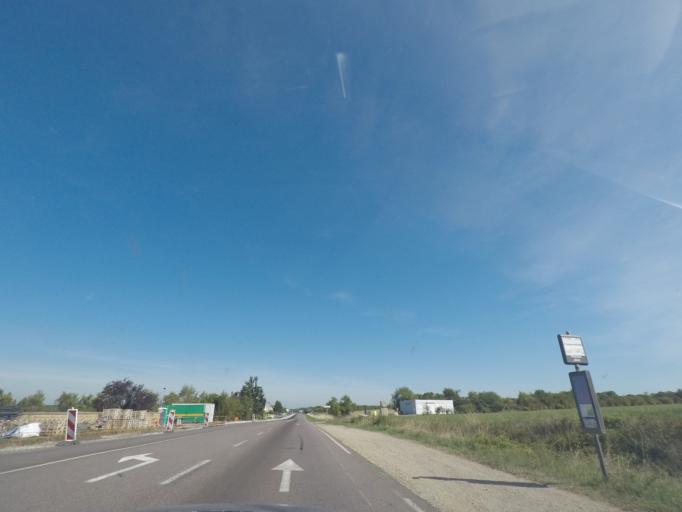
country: FR
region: Lorraine
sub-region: Departement de la Moselle
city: Hettange-Grande
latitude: 49.4114
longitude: 6.1549
